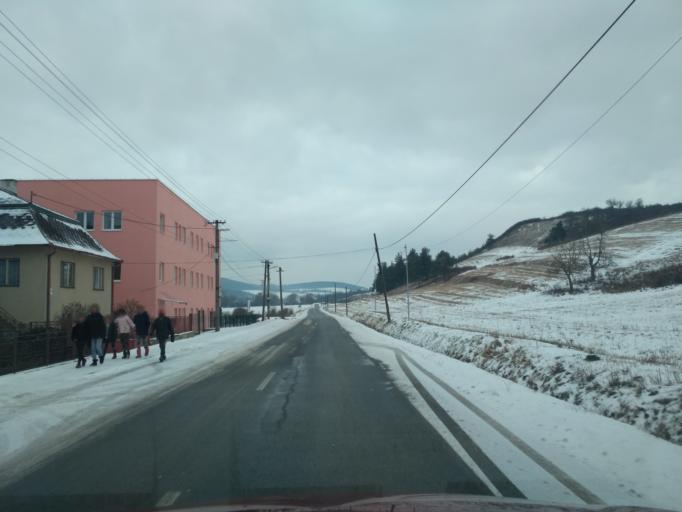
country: SK
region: Presovsky
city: Sabinov
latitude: 49.0161
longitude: 21.1182
